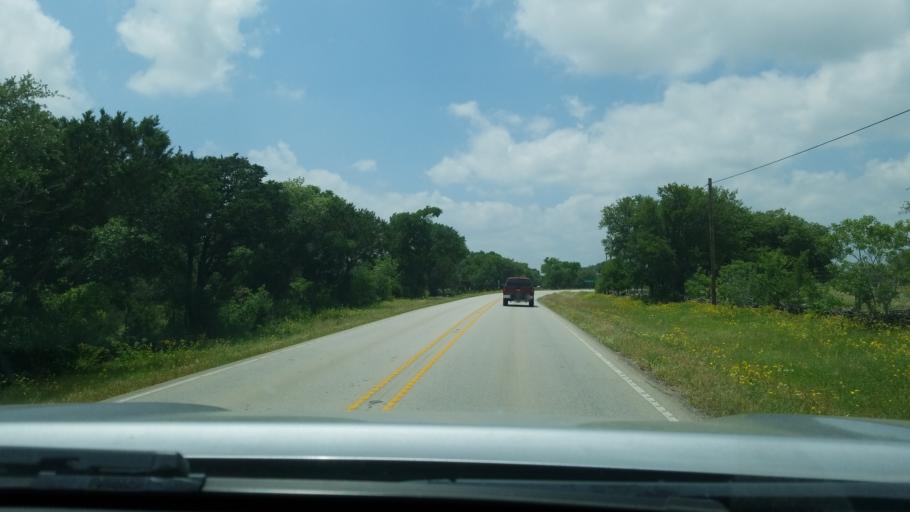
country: US
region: Texas
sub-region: Hays County
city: Dripping Springs
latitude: 30.1321
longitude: -98.0230
